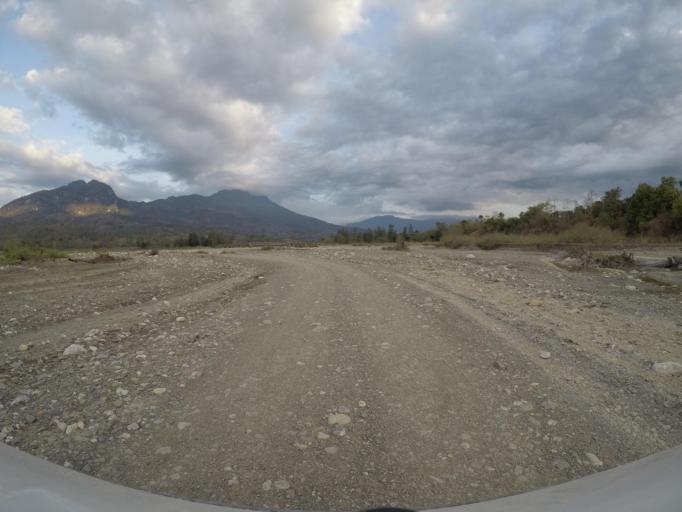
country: TL
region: Bobonaro
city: Maliana
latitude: -8.9089
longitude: 125.2125
